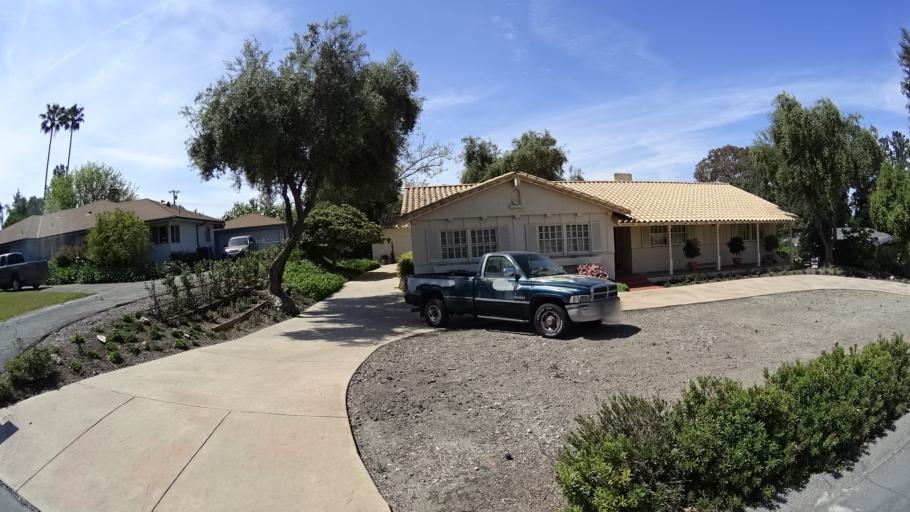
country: US
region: California
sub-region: Ventura County
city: Thousand Oaks
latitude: 34.1955
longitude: -118.8526
